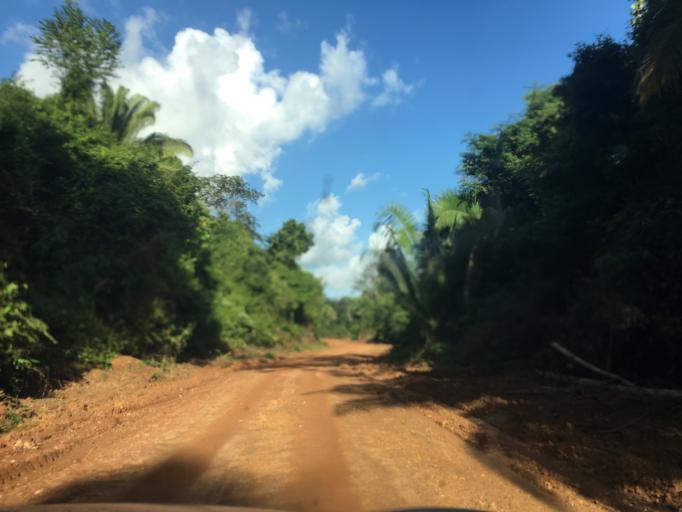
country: BZ
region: Stann Creek
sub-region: Dangriga
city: Dangriga
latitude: 16.7979
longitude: -88.4092
